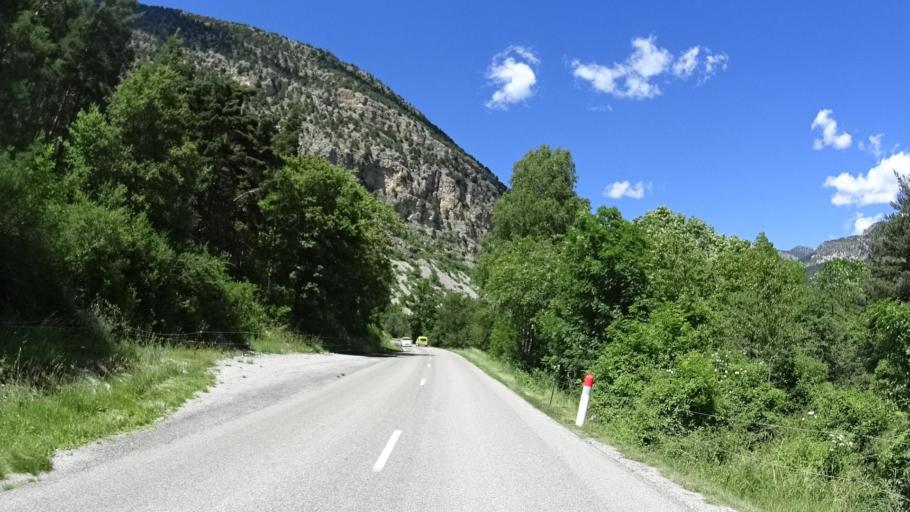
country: FR
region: Provence-Alpes-Cote d'Azur
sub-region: Departement des Alpes-de-Haute-Provence
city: Annot
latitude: 44.1006
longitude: 6.5686
